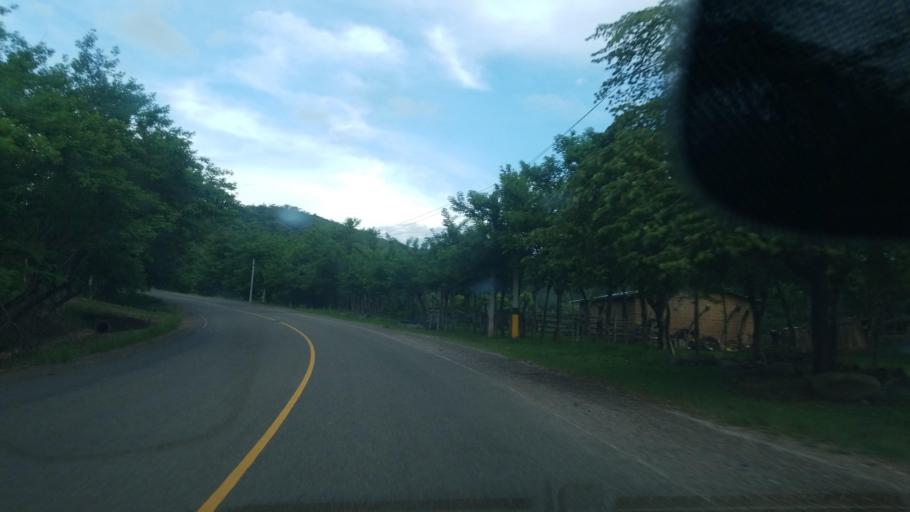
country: HN
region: Santa Barbara
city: Concepcion del Sur
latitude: 14.8010
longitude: -88.1769
